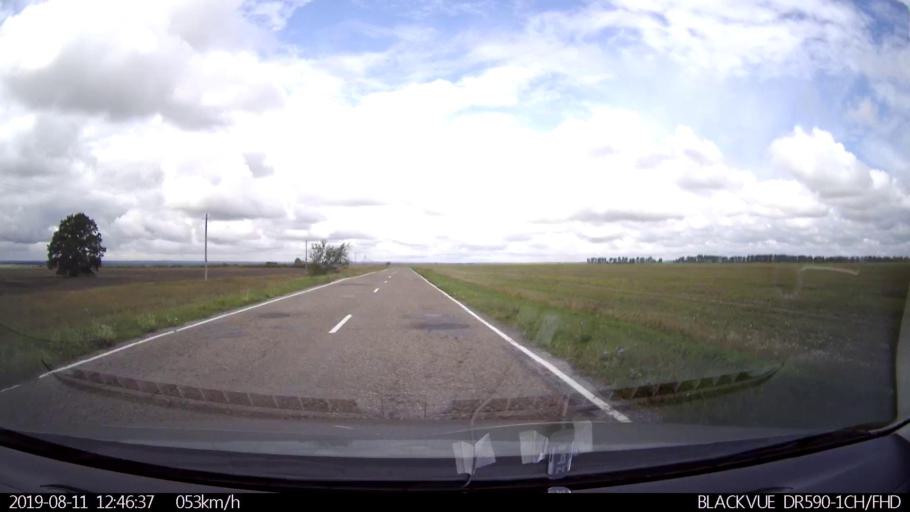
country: RU
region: Ulyanovsk
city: Ignatovka
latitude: 53.8652
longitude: 47.7170
